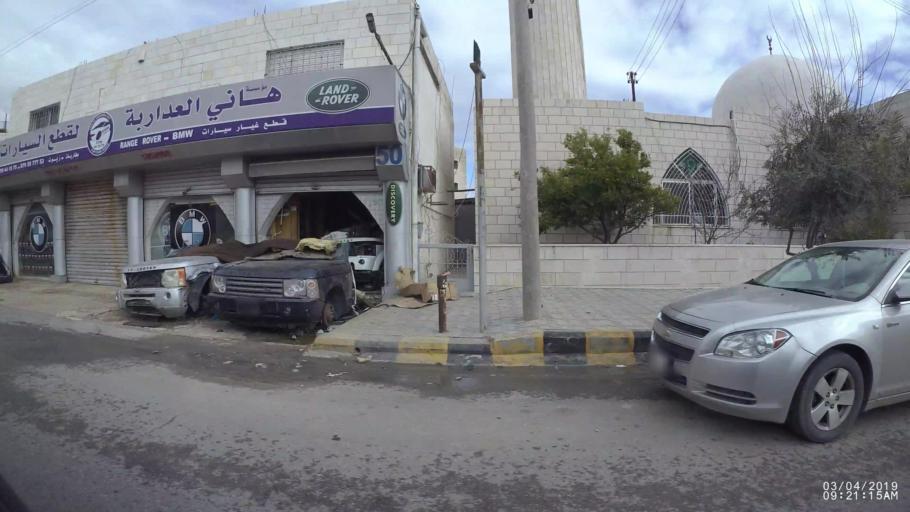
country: JO
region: Amman
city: Wadi as Sir
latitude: 31.9460
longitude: 35.8415
